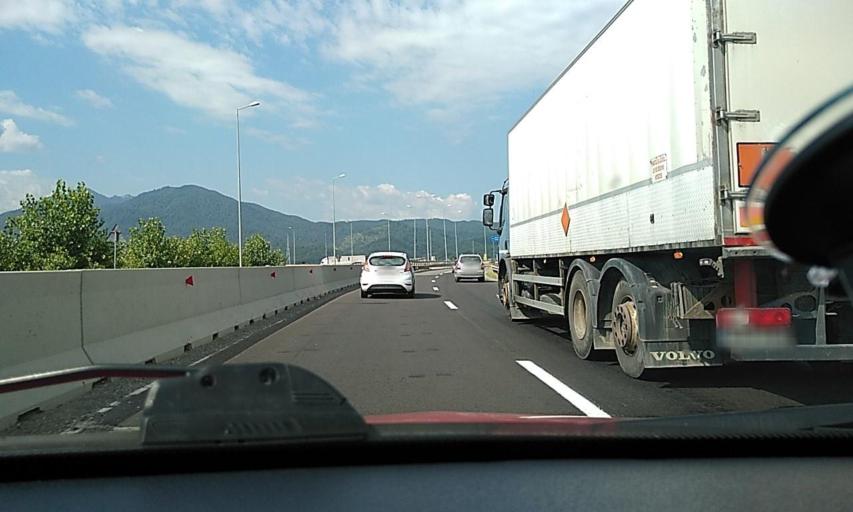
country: RO
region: Brasov
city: Brasov
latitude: 45.6392
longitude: 25.6594
